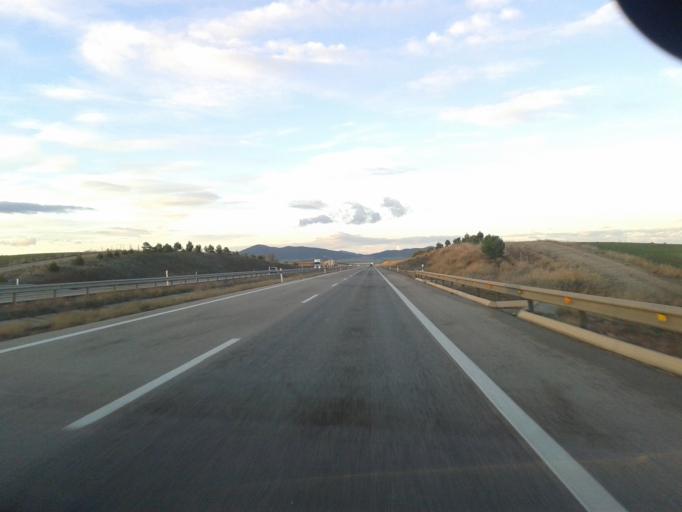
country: ES
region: Aragon
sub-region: Provincia de Zaragoza
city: Romanos
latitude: 41.1398
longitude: -1.2903
